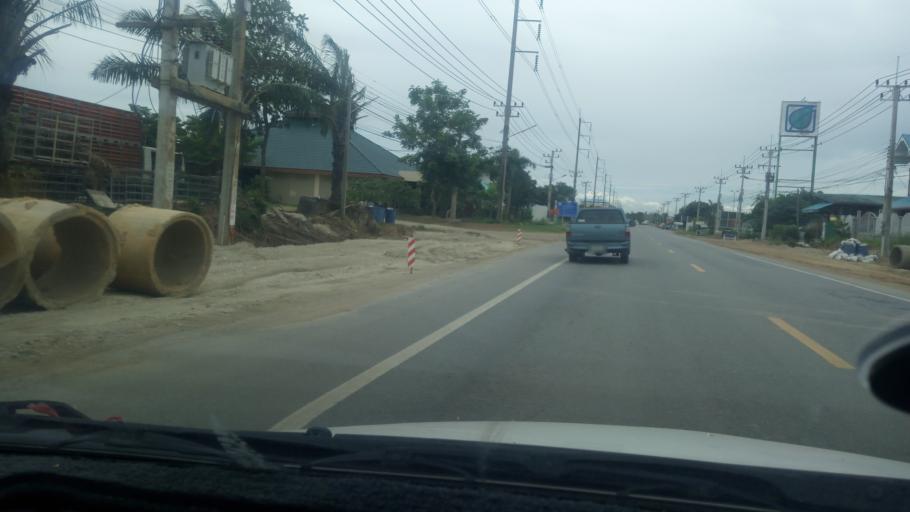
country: TH
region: Chon Buri
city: Phanat Nikhom
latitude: 13.5140
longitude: 101.1559
